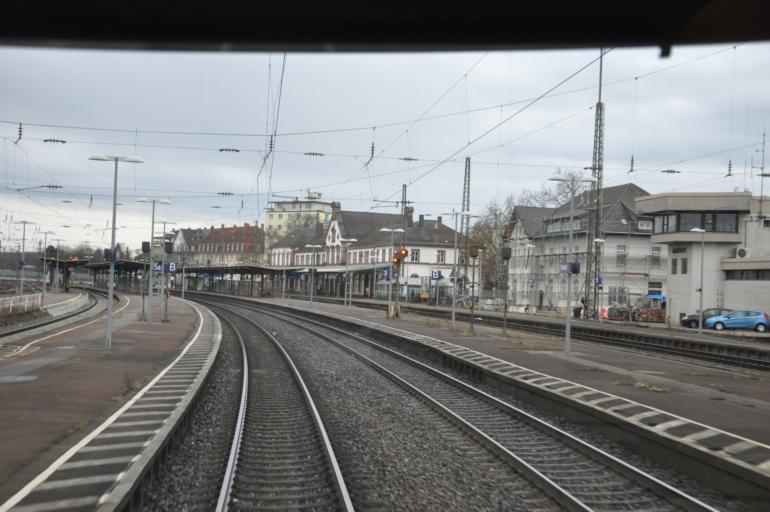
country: DE
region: Baden-Wuerttemberg
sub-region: Karlsruhe Region
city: Rastatt
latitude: 48.8620
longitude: 8.2174
